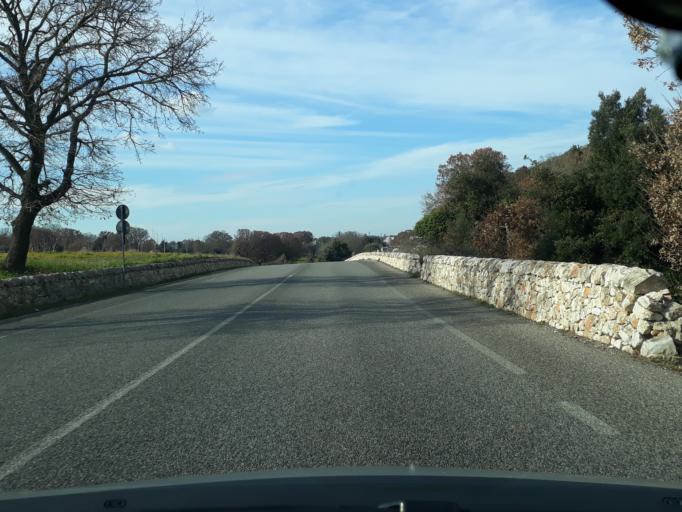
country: IT
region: Apulia
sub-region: Provincia di Bari
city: Locorotondo
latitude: 40.7595
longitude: 17.3392
